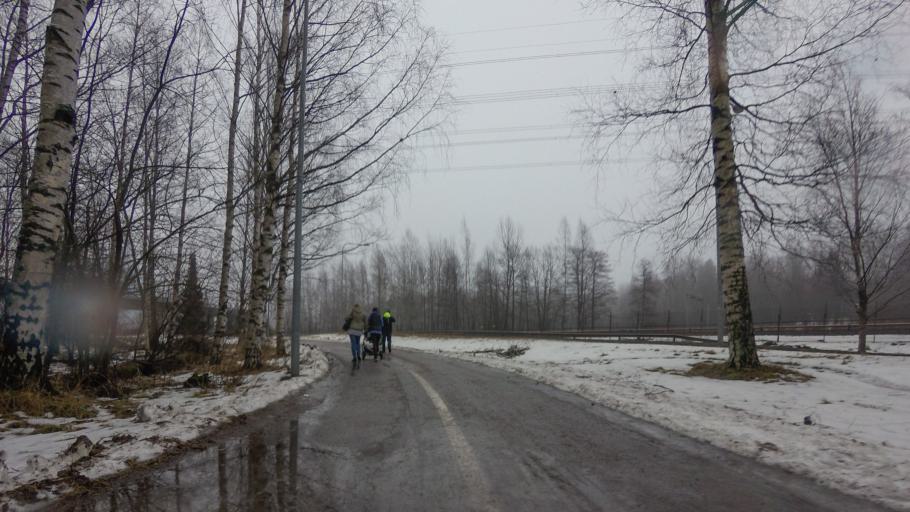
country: FI
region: Uusimaa
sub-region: Helsinki
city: Vantaa
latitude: 60.2088
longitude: 25.0641
